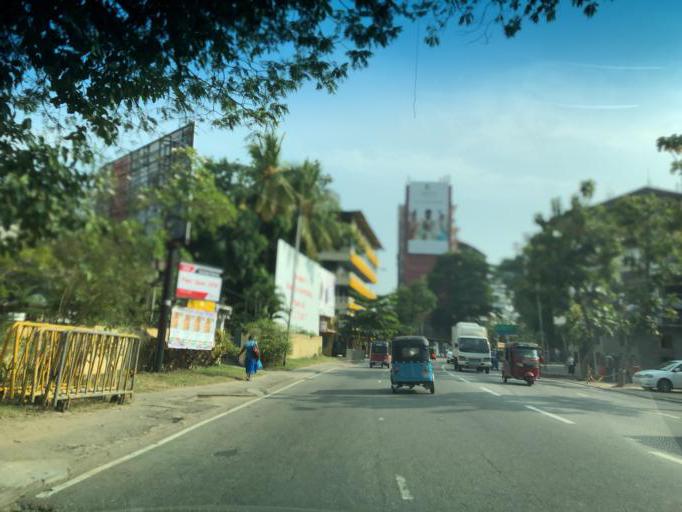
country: LK
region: Western
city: Colombo
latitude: 6.9163
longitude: 79.8558
